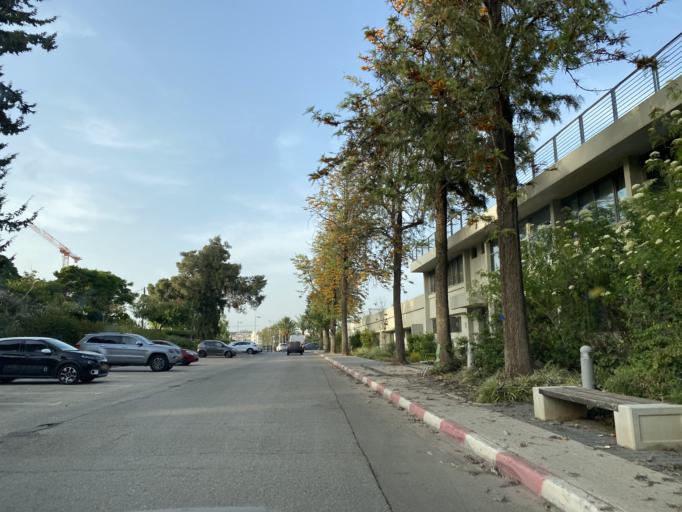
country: IL
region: Tel Aviv
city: Herzliyya
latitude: 32.1583
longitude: 34.8323
